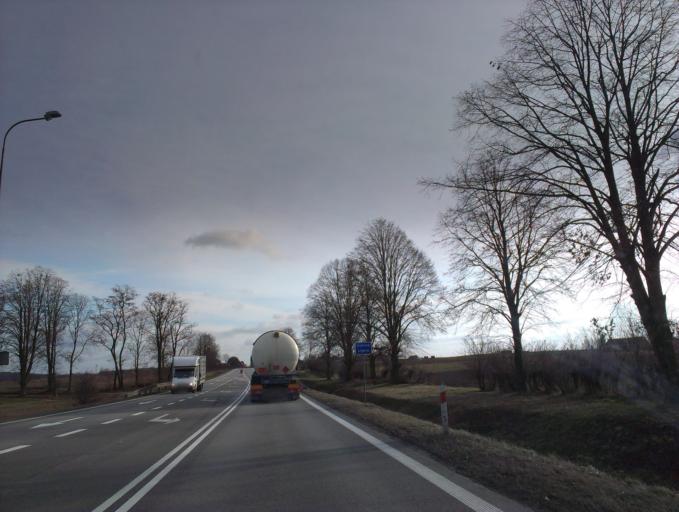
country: PL
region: Kujawsko-Pomorskie
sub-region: Powiat lipnowski
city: Kikol
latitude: 52.8862
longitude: 19.1322
